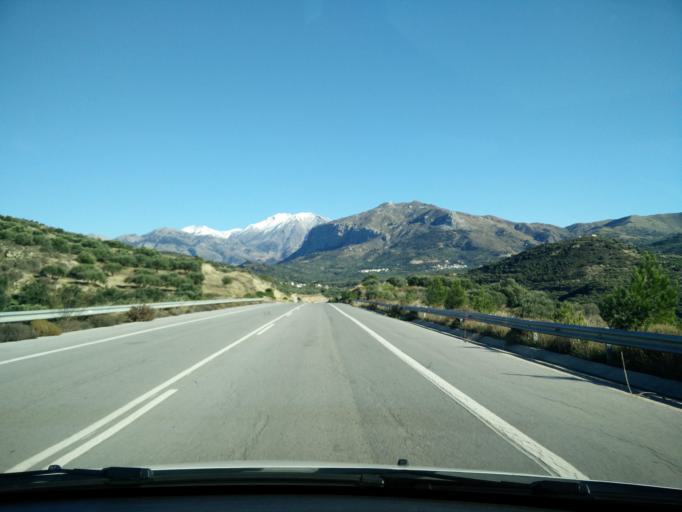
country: GR
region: Crete
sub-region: Nomos Irakleiou
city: Arkalochori
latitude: 35.0802
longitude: 25.3214
